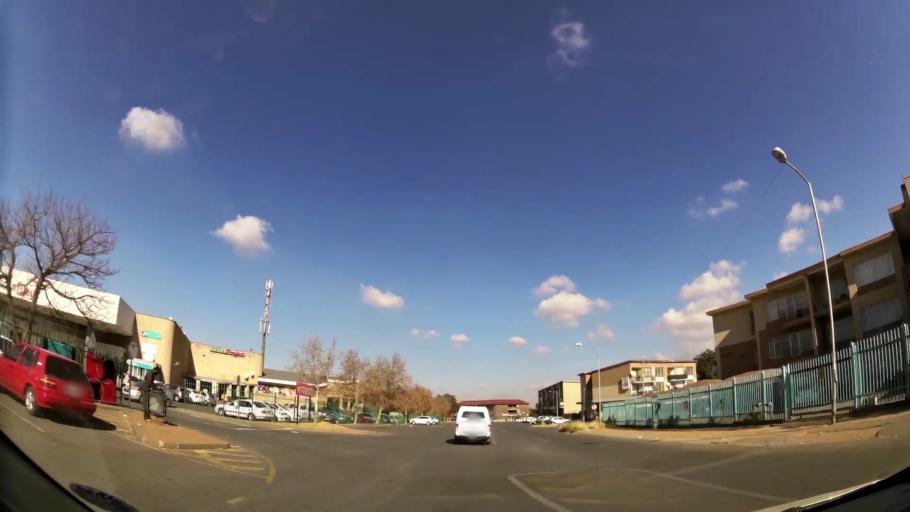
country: ZA
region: Gauteng
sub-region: City of Johannesburg Metropolitan Municipality
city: Roodepoort
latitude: -26.1403
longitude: 27.8316
